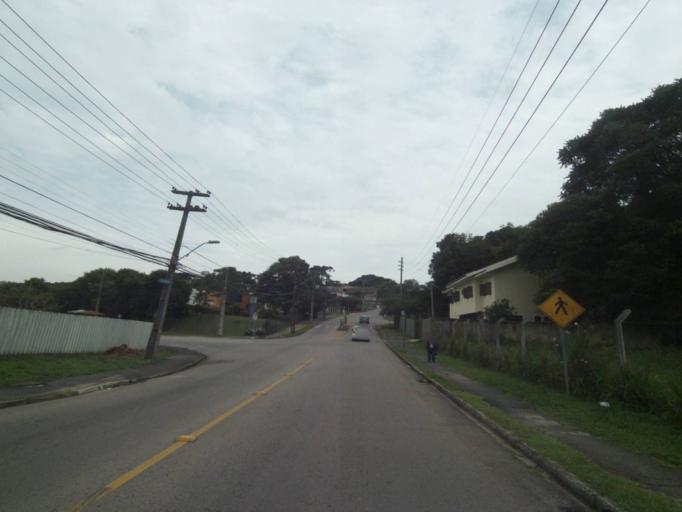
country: BR
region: Parana
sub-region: Curitiba
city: Curitiba
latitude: -25.4132
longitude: -49.3020
